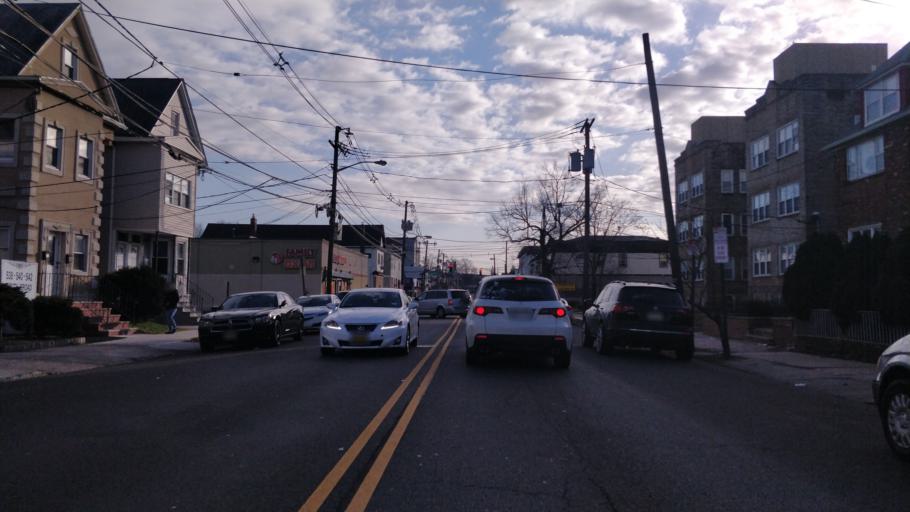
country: US
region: New Jersey
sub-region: Union County
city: Elizabeth
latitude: 40.6515
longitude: -74.2161
